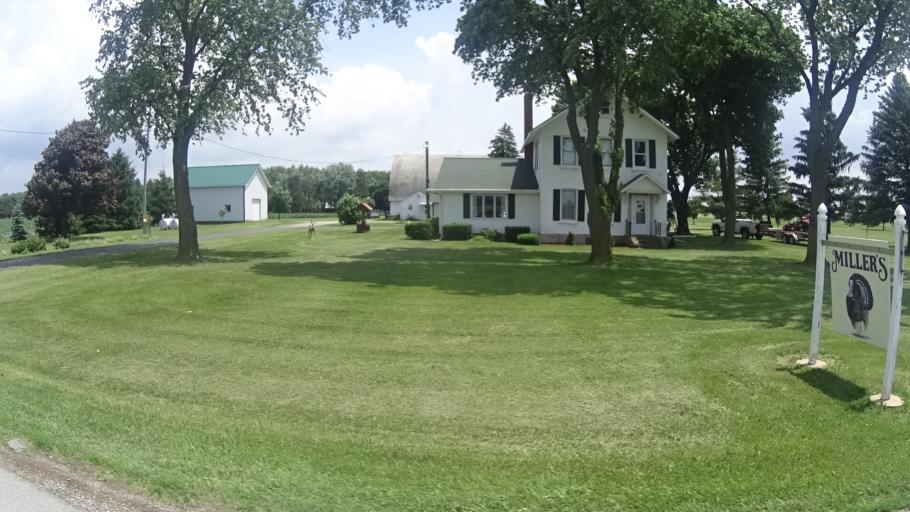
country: US
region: Ohio
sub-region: Huron County
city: Monroeville
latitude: 41.3342
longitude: -82.7474
